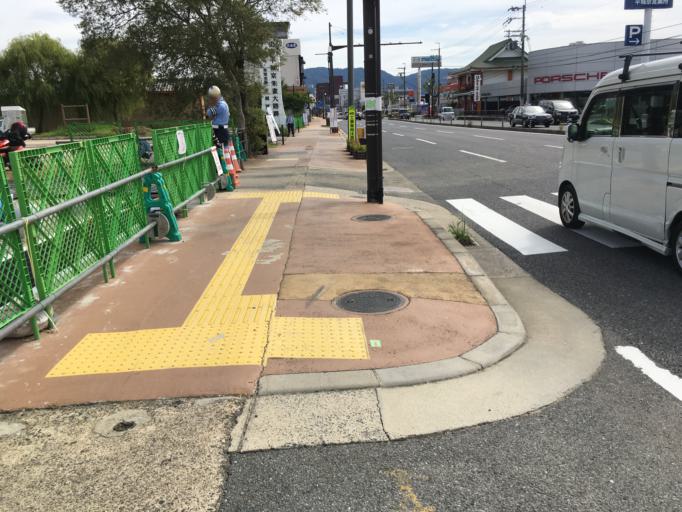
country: JP
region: Nara
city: Nara-shi
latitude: 34.6845
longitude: 135.7940
